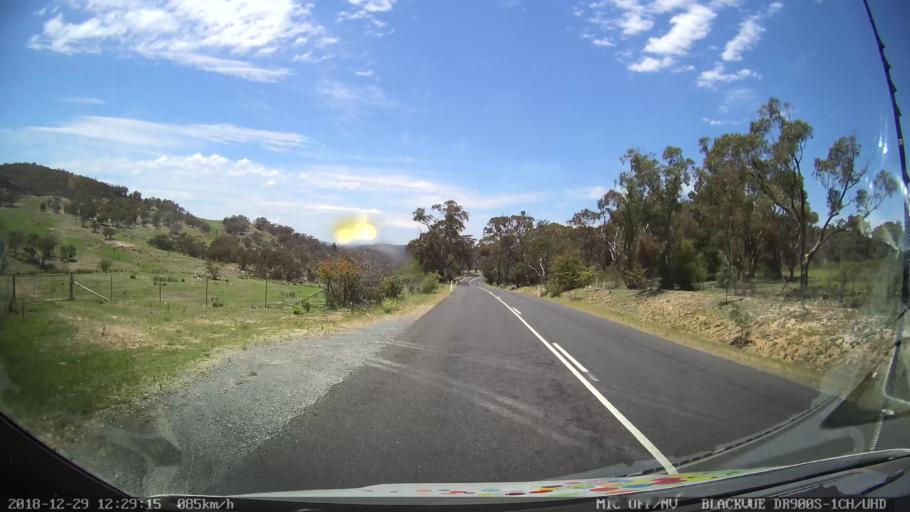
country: AU
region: Australian Capital Territory
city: Macarthur
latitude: -35.4957
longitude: 149.2298
